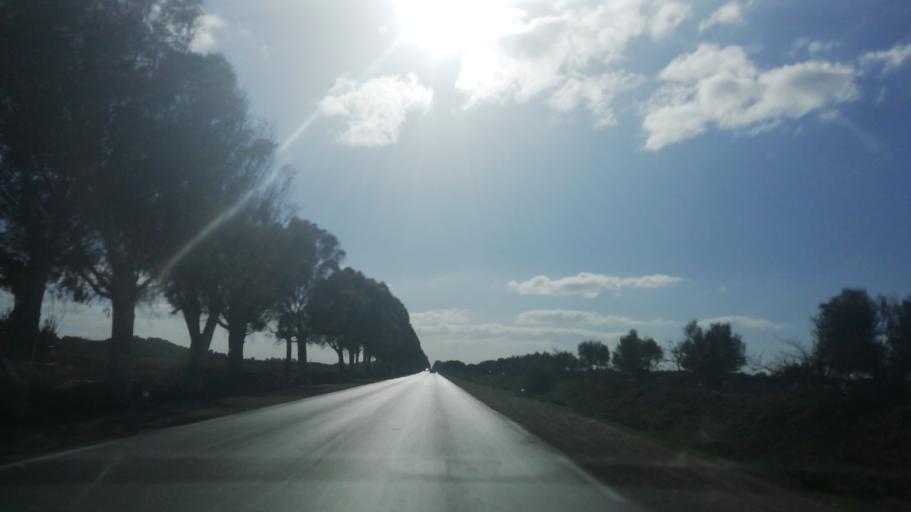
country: DZ
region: Mostaganem
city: Mostaganem
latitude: 35.9865
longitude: 0.2884
